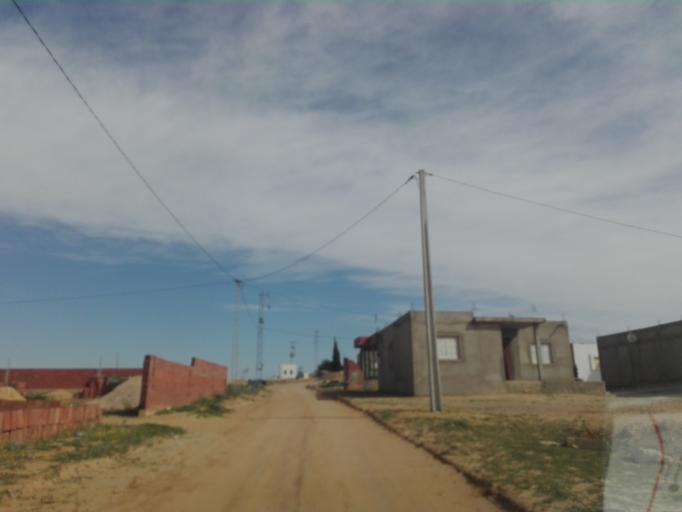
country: TN
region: Safaqis
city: Sfax
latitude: 34.7428
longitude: 10.5110
